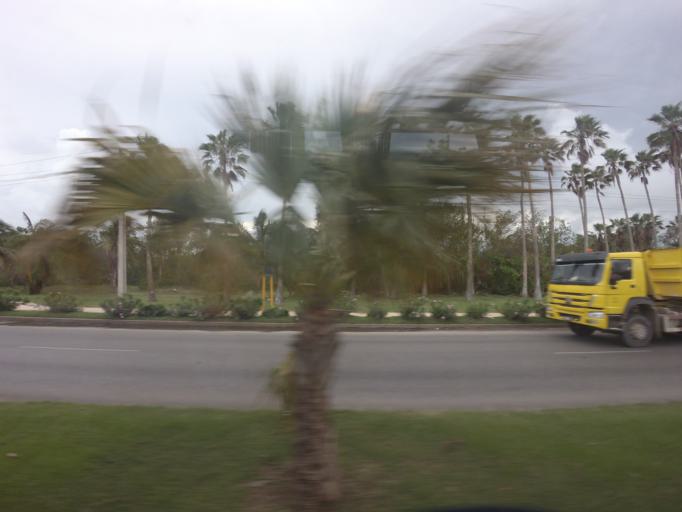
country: CU
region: Matanzas
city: Varadero
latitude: 23.1360
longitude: -81.2794
